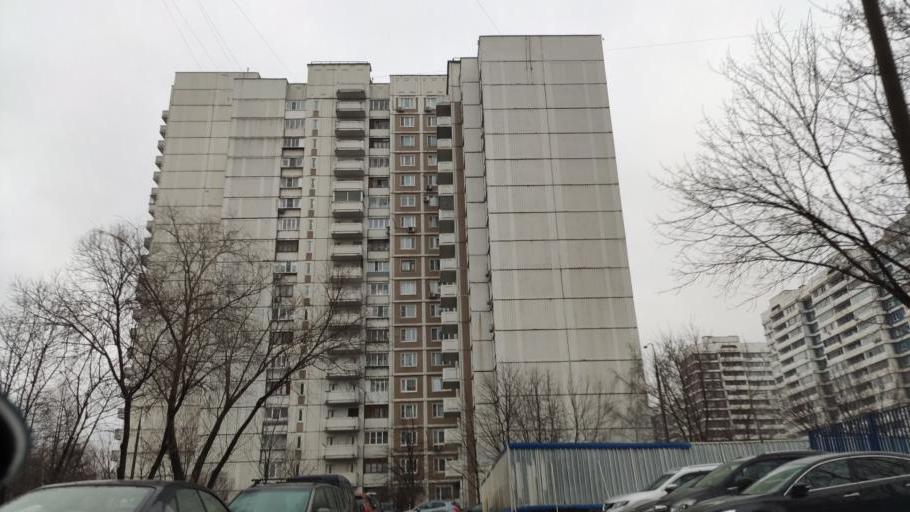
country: RU
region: Moskovskaya
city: Bol'shaya Setun'
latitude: 55.7418
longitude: 37.4338
